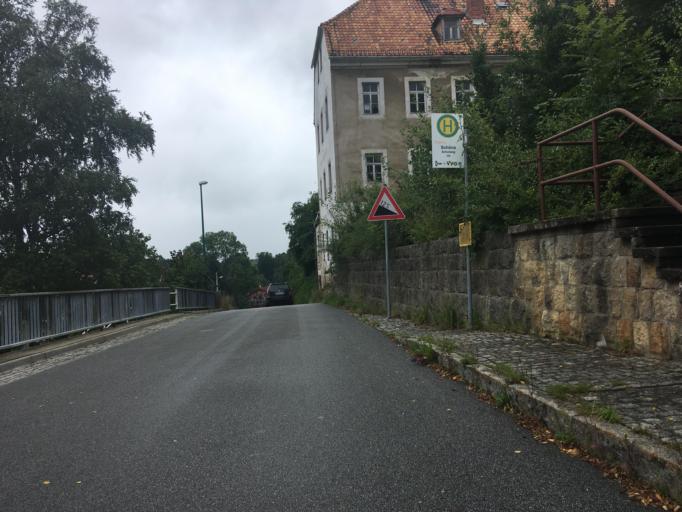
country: DE
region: Saxony
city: Bad Schandau
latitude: 50.8860
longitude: 14.2112
